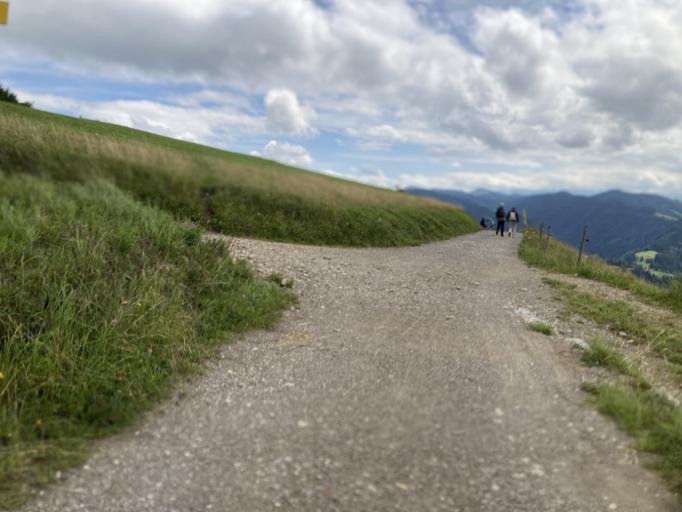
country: CH
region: Thurgau
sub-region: Muenchwilen District
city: Fischingen
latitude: 47.3704
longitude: 8.9417
